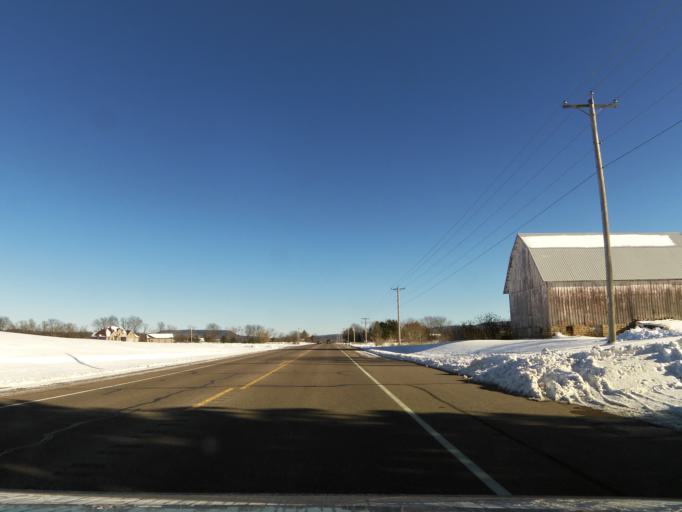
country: US
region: Wisconsin
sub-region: Sauk County
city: Baraboo
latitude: 43.4743
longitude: -89.6697
